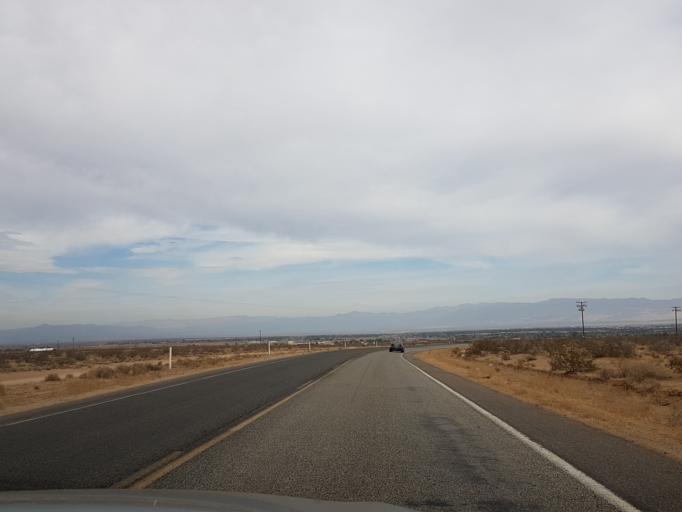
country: US
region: California
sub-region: Kern County
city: Ridgecrest
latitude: 35.5779
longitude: -117.7125
